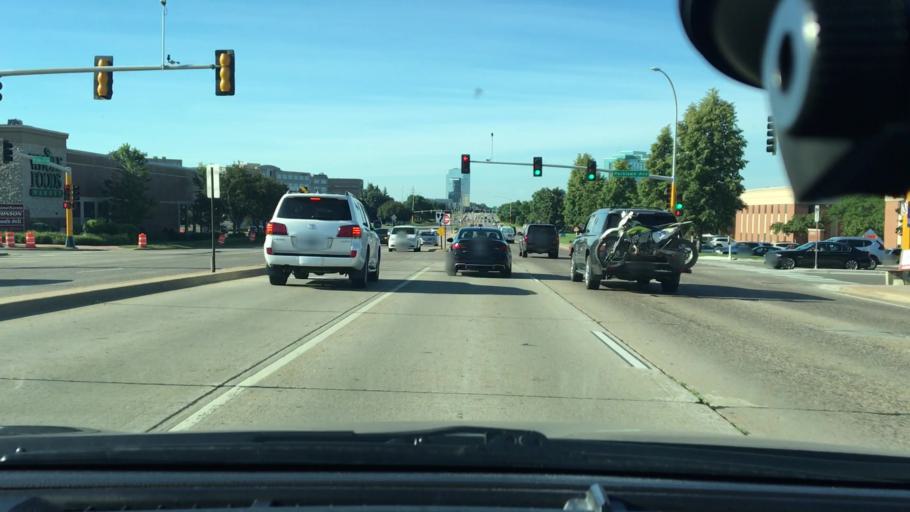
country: US
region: Minnesota
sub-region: Hennepin County
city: Edina
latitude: 44.8686
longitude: -93.3290
